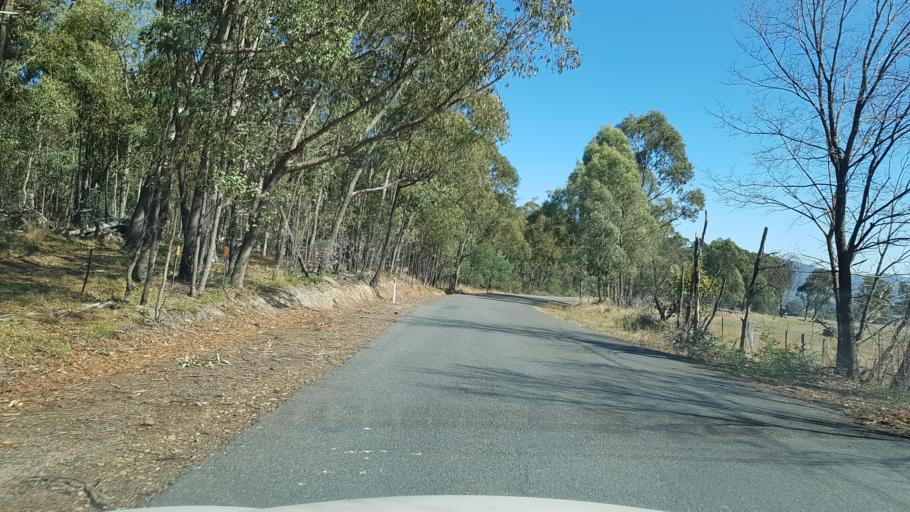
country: AU
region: Victoria
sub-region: Mansfield
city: Mansfield
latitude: -36.8163
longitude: 146.4649
